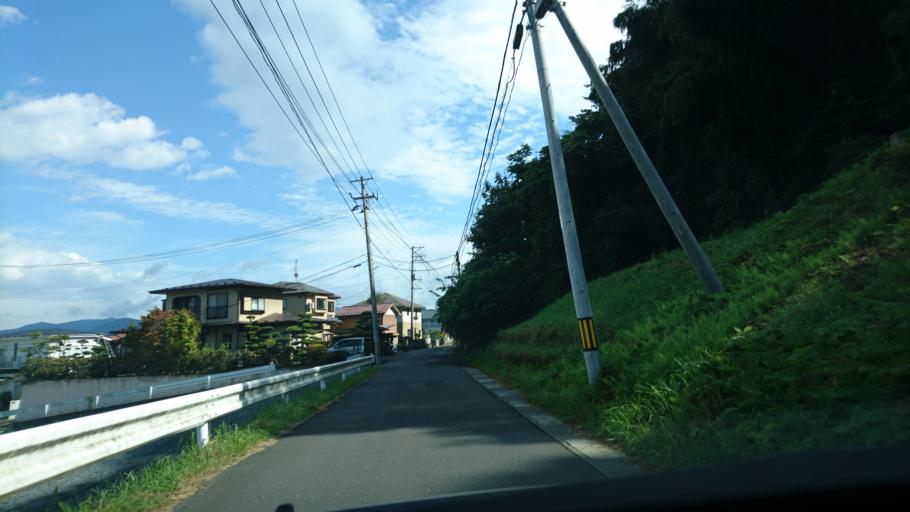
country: JP
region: Iwate
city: Ichinoseki
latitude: 38.9254
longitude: 141.1510
